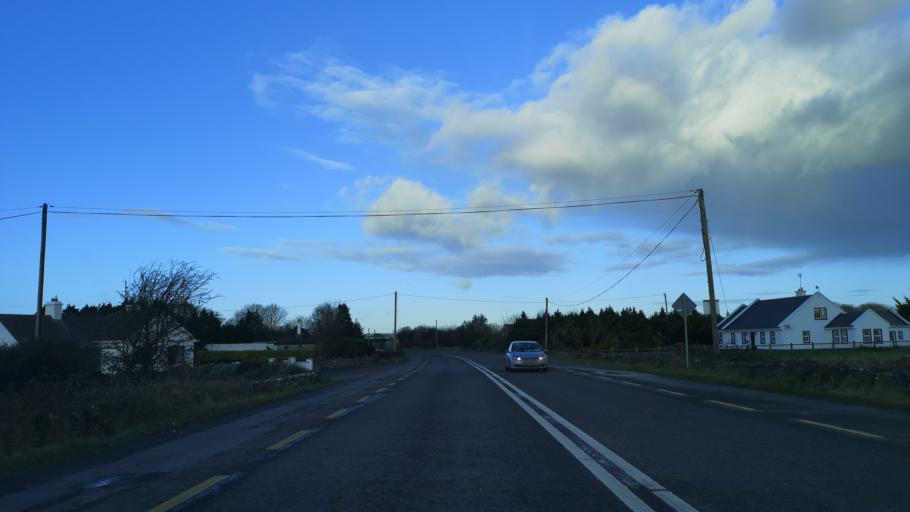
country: IE
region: Connaught
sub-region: County Galway
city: Oranmore
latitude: 53.2855
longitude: -8.9253
